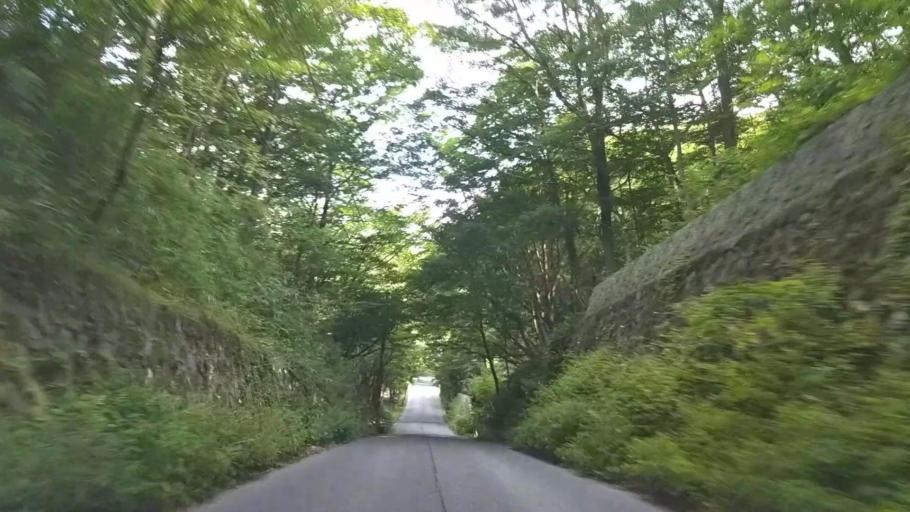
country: JP
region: Kanagawa
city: Hakone
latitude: 35.2533
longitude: 139.0341
